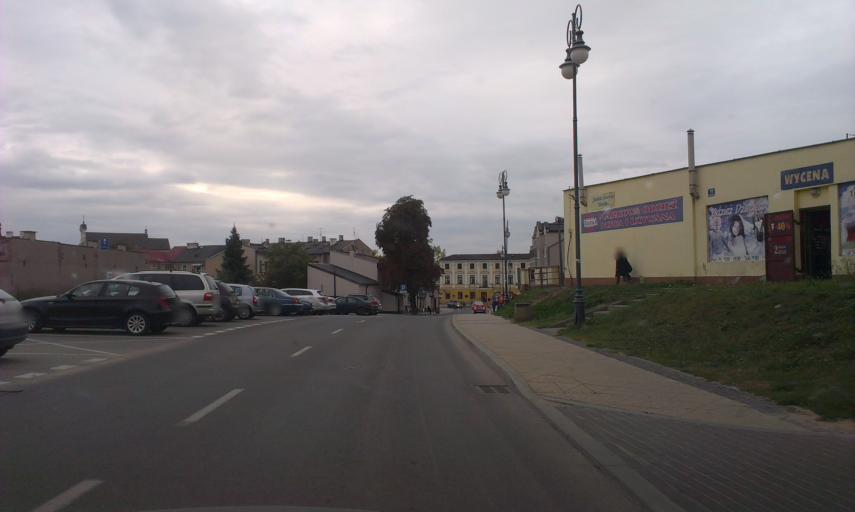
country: PL
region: Masovian Voivodeship
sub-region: Radom
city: Radom
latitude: 51.4028
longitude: 21.1511
